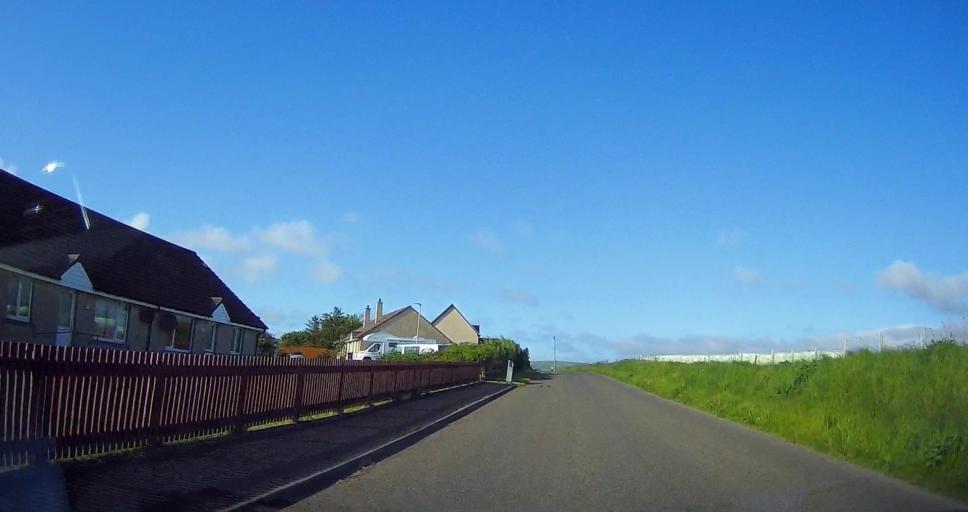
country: GB
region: Scotland
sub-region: Orkney Islands
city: Stromness
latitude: 59.0698
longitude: -3.2281
